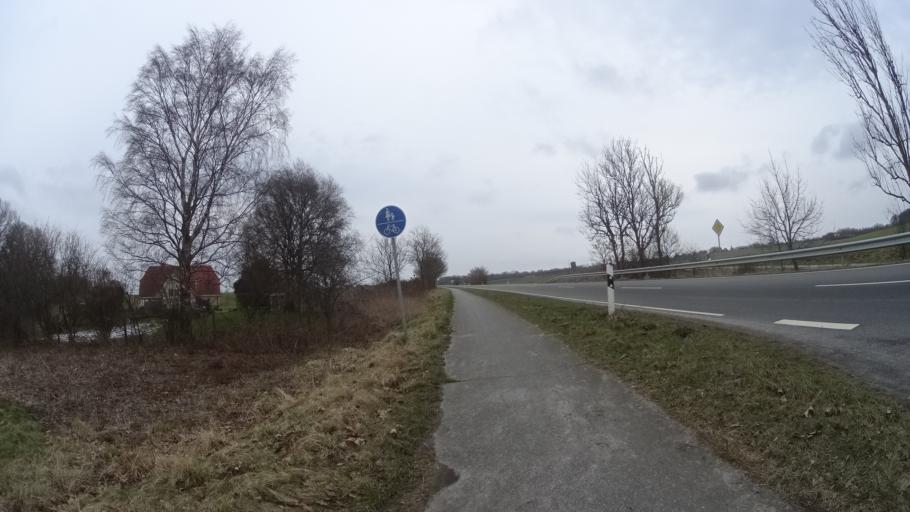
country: DE
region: Schleswig-Holstein
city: Stakendorf
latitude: 54.3770
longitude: 10.4607
